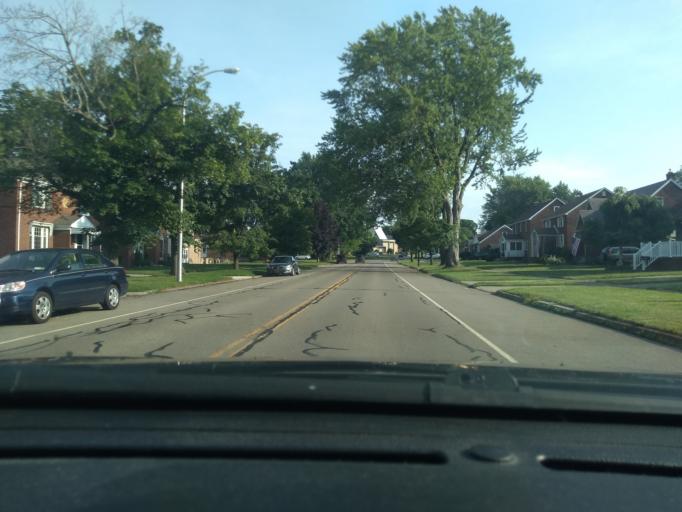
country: US
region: New York
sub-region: Erie County
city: Lackawanna
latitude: 42.8306
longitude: -78.8086
